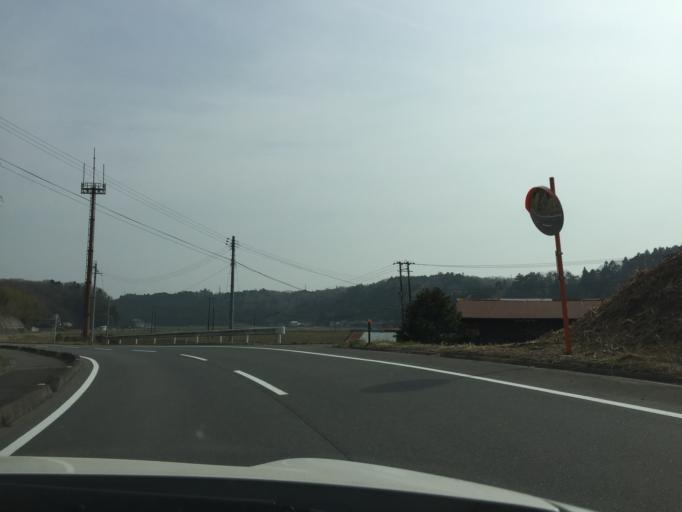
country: JP
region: Fukushima
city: Iwaki
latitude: 36.9772
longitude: 140.8009
